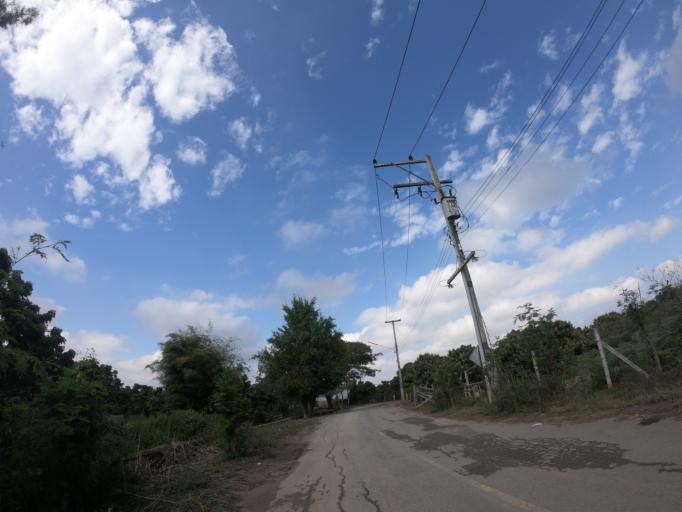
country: TH
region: Chiang Mai
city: Saraphi
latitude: 18.7037
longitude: 98.9767
